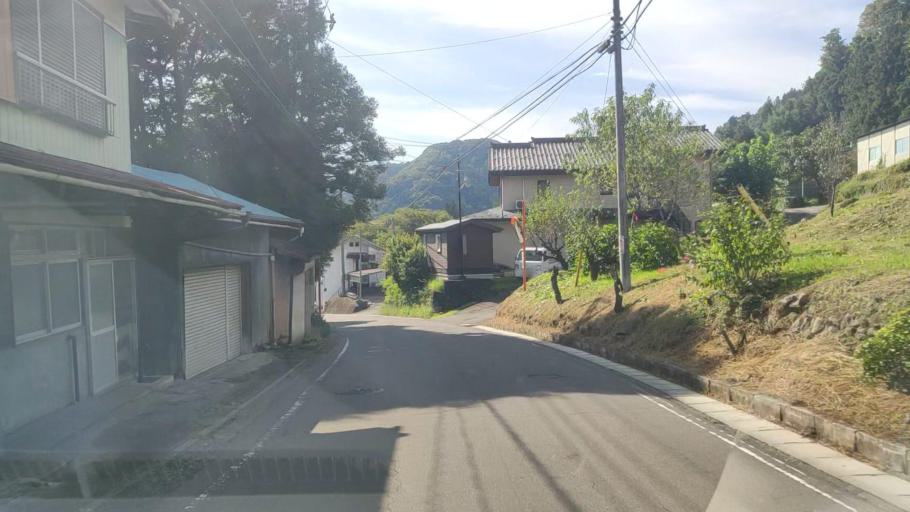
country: JP
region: Gunma
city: Nakanojomachi
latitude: 36.6189
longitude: 138.7795
